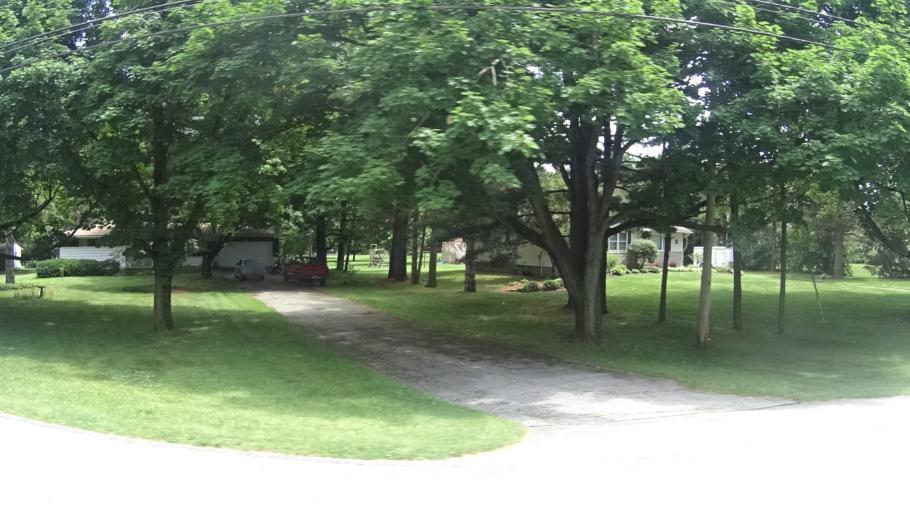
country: US
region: Ohio
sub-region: Erie County
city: Milan
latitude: 41.3027
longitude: -82.5871
